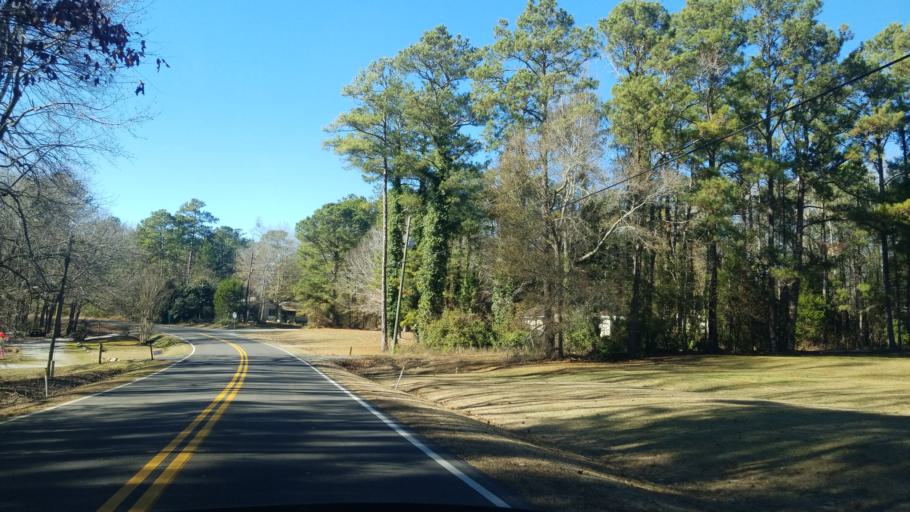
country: US
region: Georgia
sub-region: Harris County
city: Hamilton
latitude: 32.6679
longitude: -84.8765
